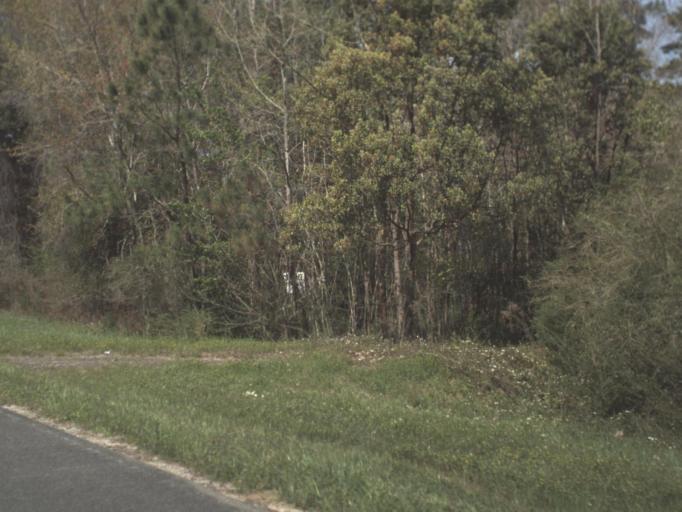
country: US
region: Florida
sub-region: Holmes County
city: Bonifay
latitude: 30.7915
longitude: -85.7429
